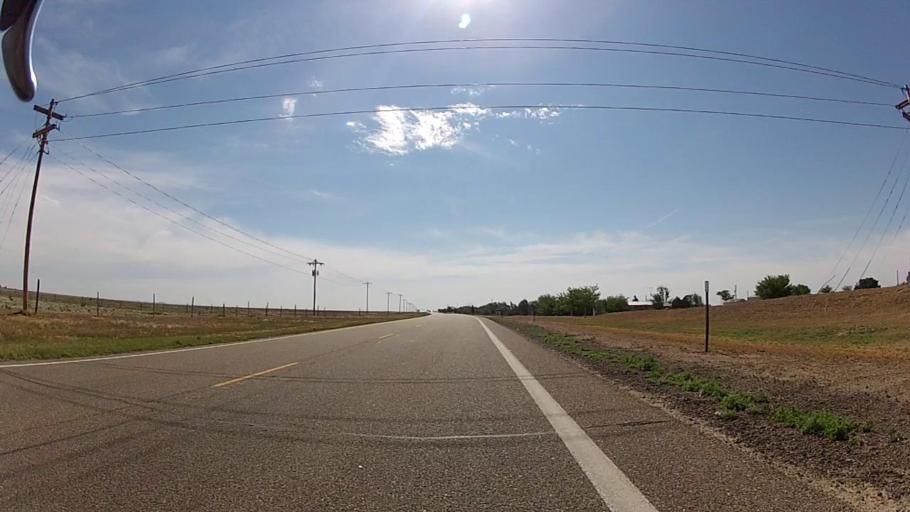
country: US
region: Kansas
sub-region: Grant County
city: Ulysses
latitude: 37.5618
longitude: -101.3005
